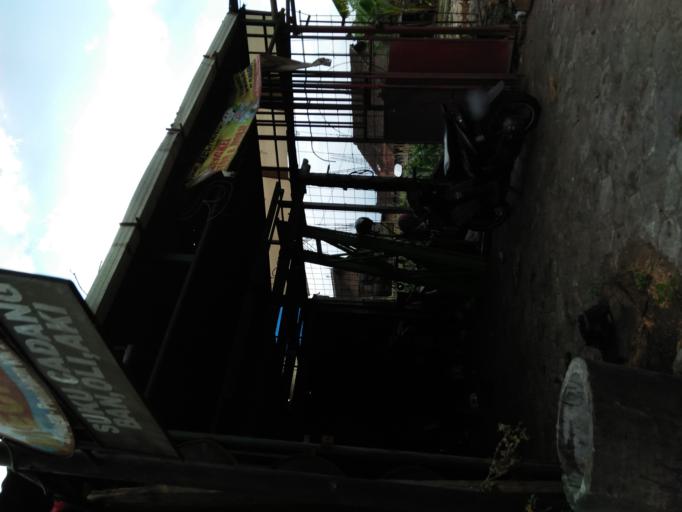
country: ID
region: Central Java
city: Candi Prambanan
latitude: -7.8306
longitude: 110.4779
